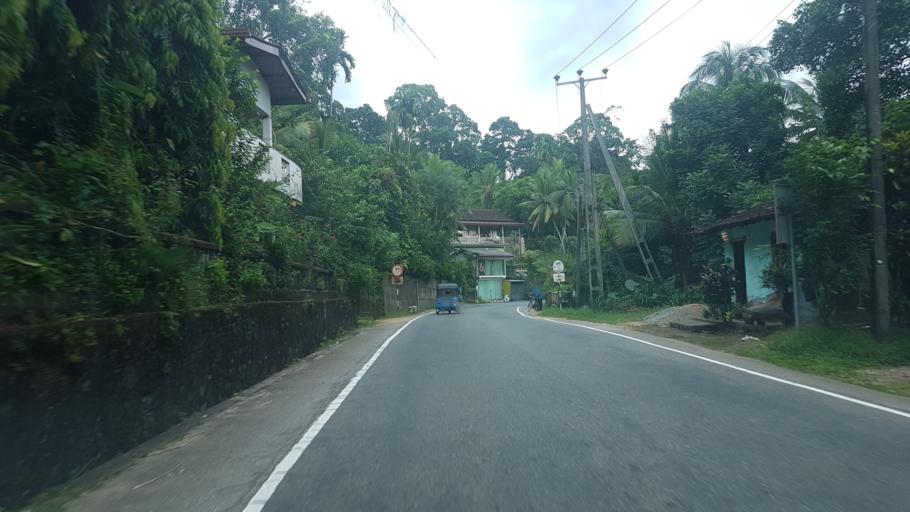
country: LK
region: Western
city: Hanwella Ihala
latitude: 7.0240
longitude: 80.2657
